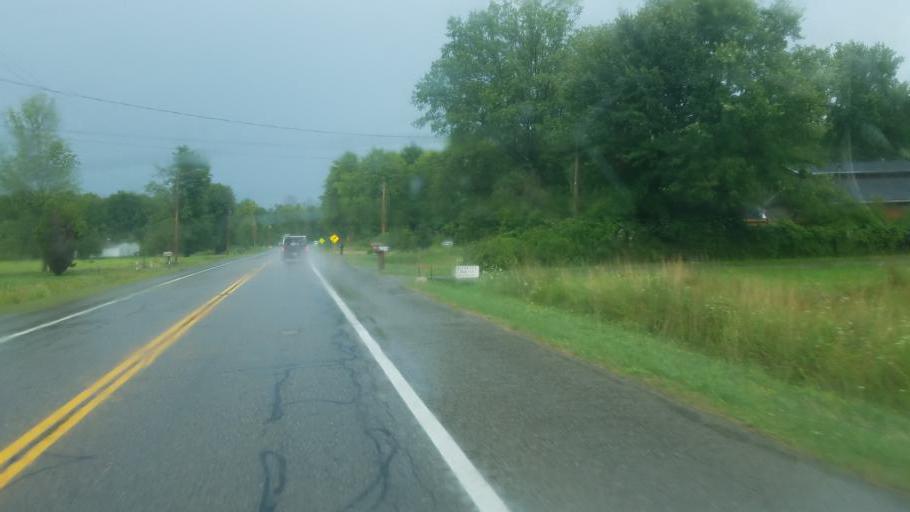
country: US
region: Ohio
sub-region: Ashtabula County
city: Orwell
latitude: 41.4611
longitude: -80.9118
